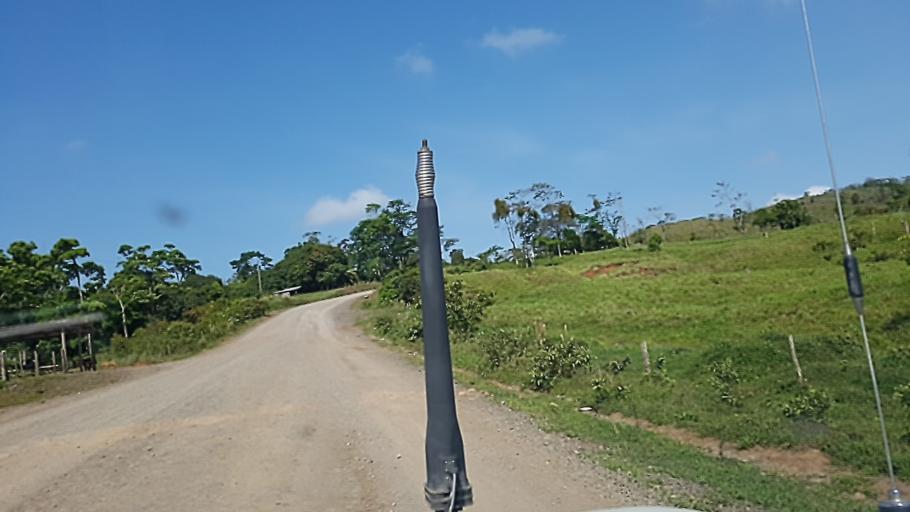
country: NI
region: Atlantico Sur
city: Nueva Guinea
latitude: 11.7887
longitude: -84.1628
